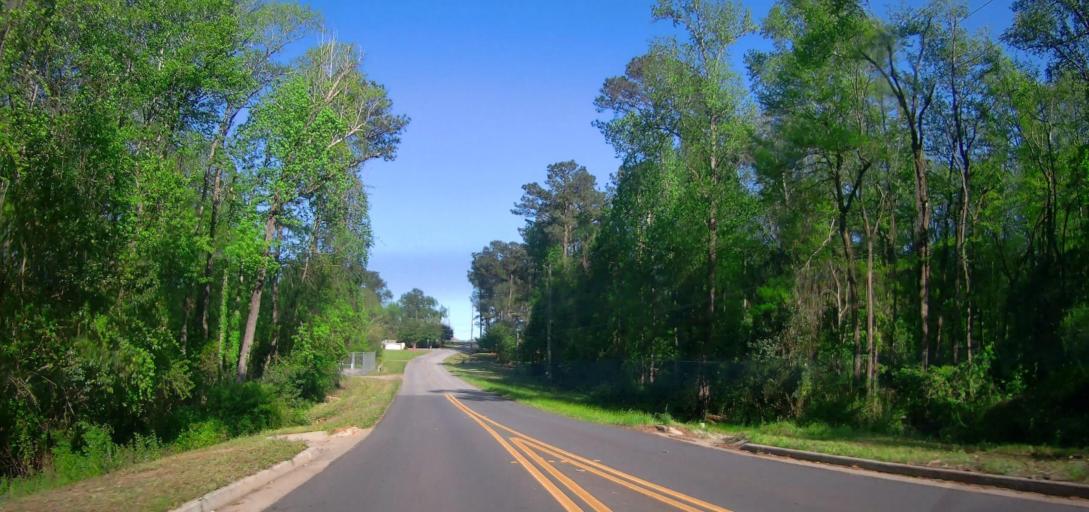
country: US
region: Georgia
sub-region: Houston County
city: Robins Air Force Base
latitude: 32.5353
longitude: -83.5932
